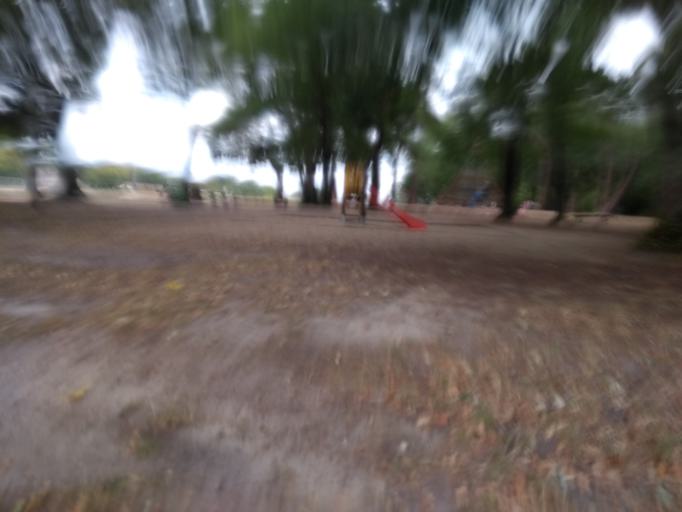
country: FR
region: Aquitaine
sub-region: Departement de la Gironde
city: Pessac
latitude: 44.8159
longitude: -0.6459
